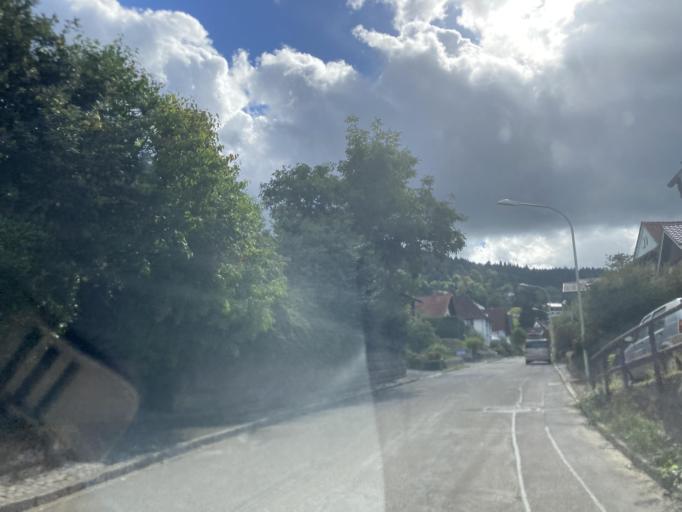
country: DE
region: Baden-Wuerttemberg
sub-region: Karlsruhe Region
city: Buhl
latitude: 48.6794
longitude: 8.1526
